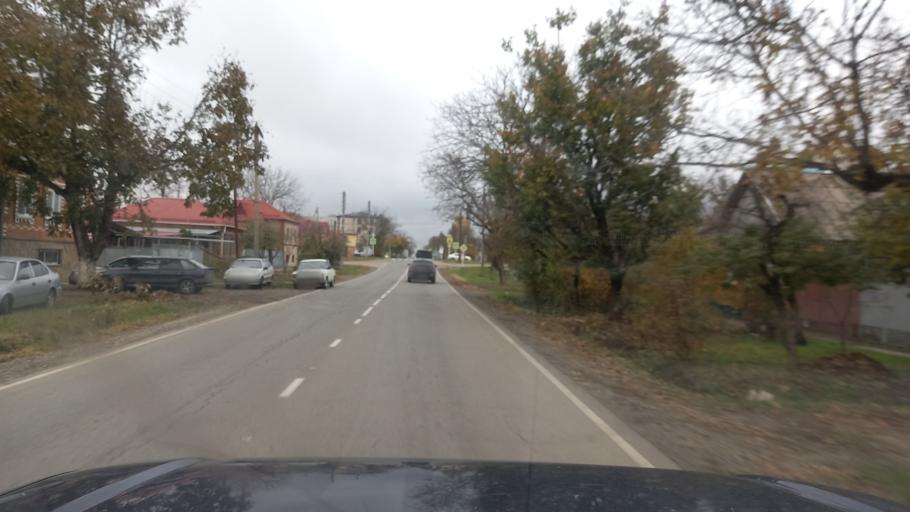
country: RU
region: Adygeya
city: Maykop
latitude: 44.6053
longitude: 40.0713
